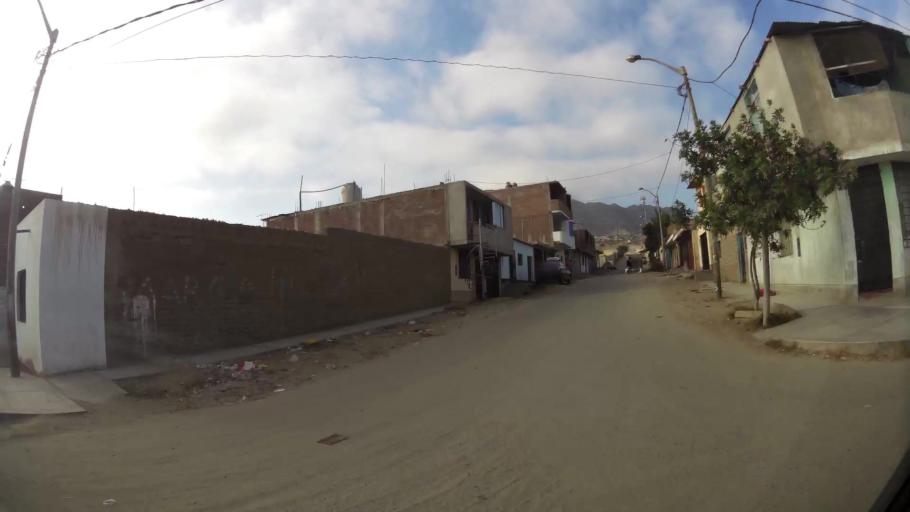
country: PE
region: La Libertad
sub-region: Provincia de Trujillo
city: La Esperanza
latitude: -8.0722
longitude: -79.0423
